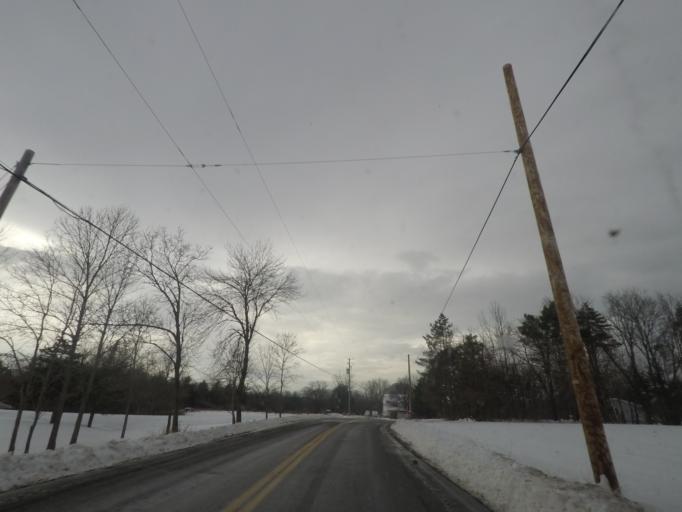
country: US
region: New York
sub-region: Rensselaer County
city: Castleton-on-Hudson
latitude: 42.5136
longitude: -73.7545
